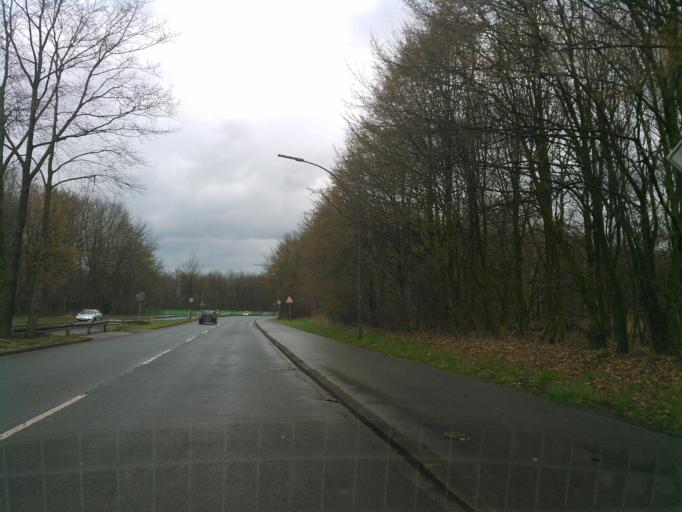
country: DE
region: North Rhine-Westphalia
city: Marl
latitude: 51.5897
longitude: 7.0611
